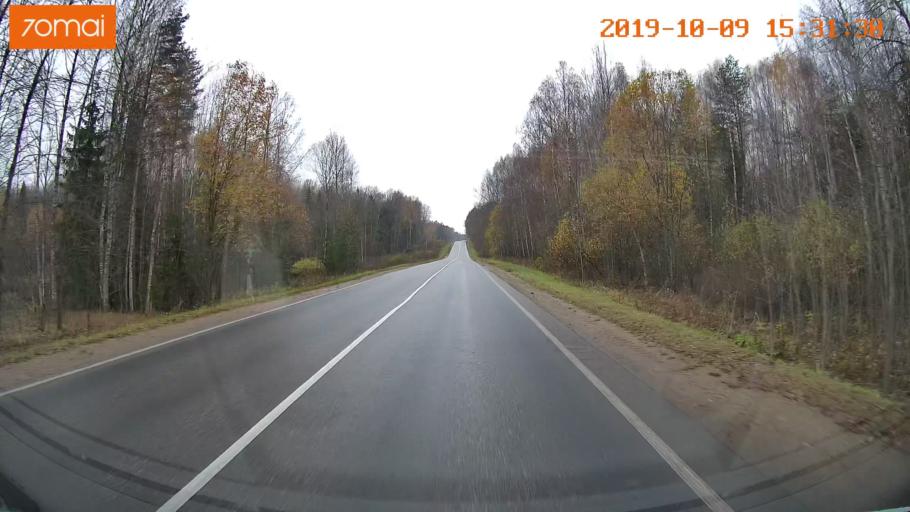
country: RU
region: Kostroma
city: Susanino
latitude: 57.9711
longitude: 41.3006
